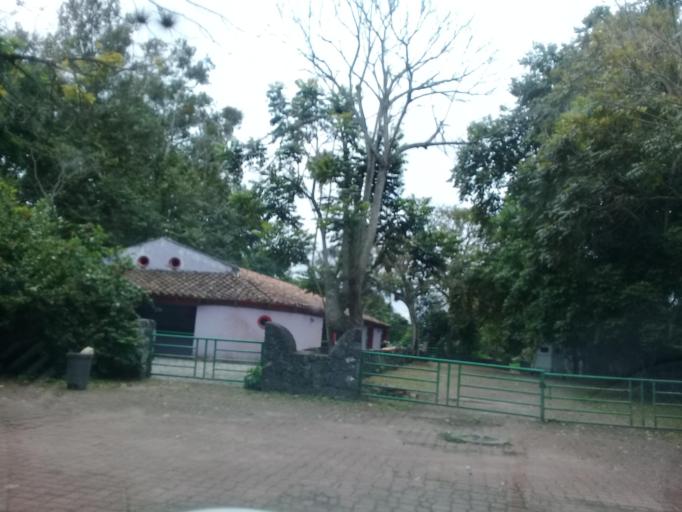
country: MX
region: Veracruz
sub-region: Xalapa
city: Colonia Santa Barbara
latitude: 19.5255
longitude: -96.8770
